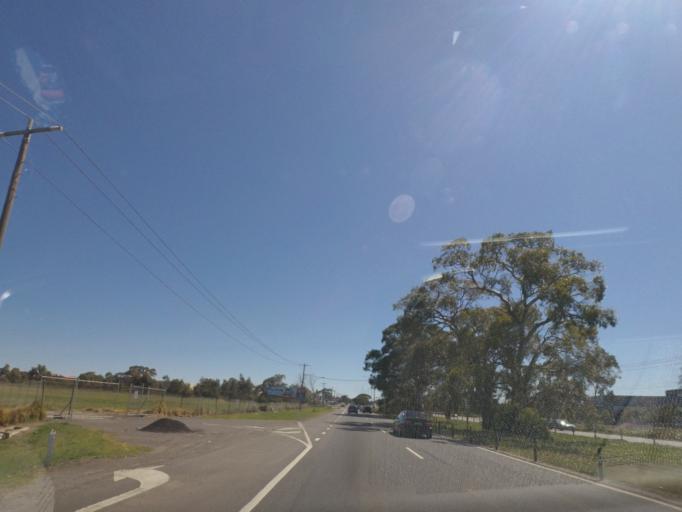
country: AU
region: Victoria
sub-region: Hume
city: Craigieburn
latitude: -37.6194
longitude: 144.9474
